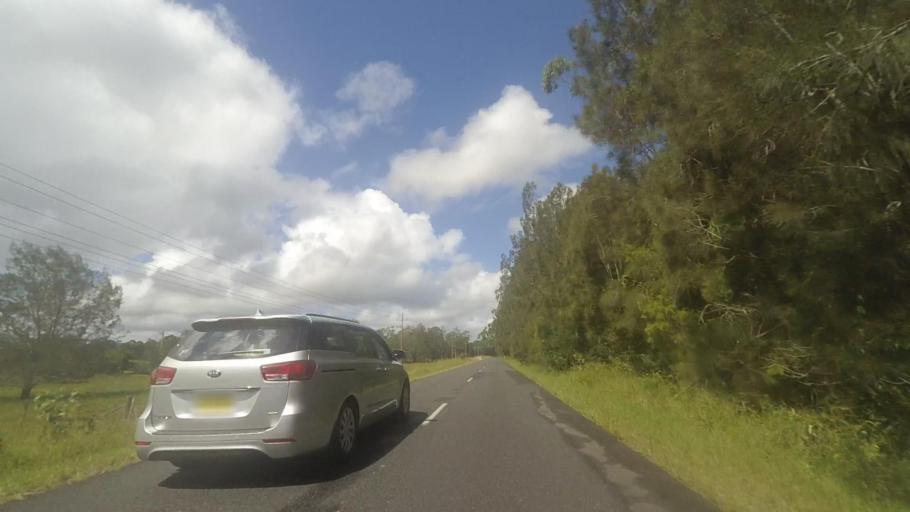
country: AU
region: New South Wales
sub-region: Great Lakes
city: Bulahdelah
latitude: -32.3901
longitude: 152.3305
